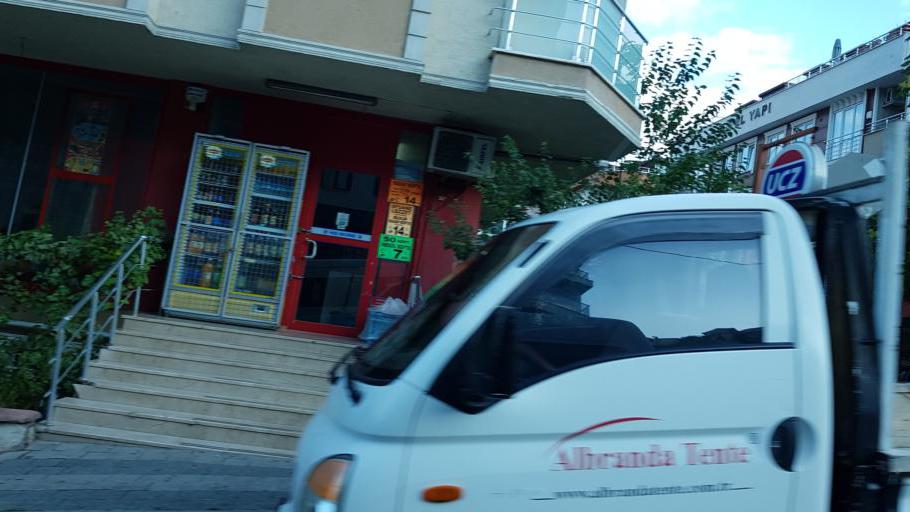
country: TR
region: Istanbul
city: Maltepe
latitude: 40.9368
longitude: 29.1545
